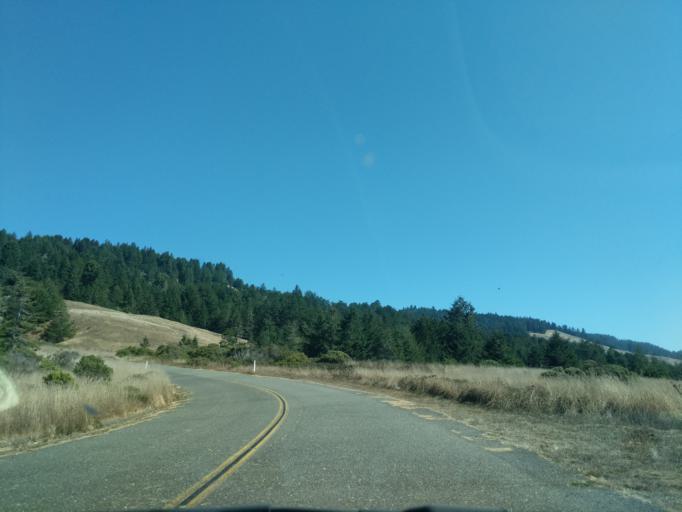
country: US
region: California
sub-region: Sonoma County
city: Monte Rio
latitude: 38.5191
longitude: -123.2450
